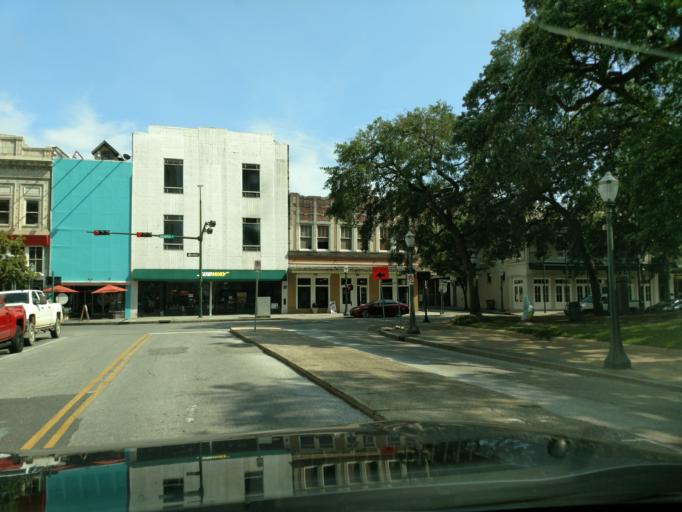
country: US
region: Alabama
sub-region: Mobile County
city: Mobile
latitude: 30.6924
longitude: -88.0419
